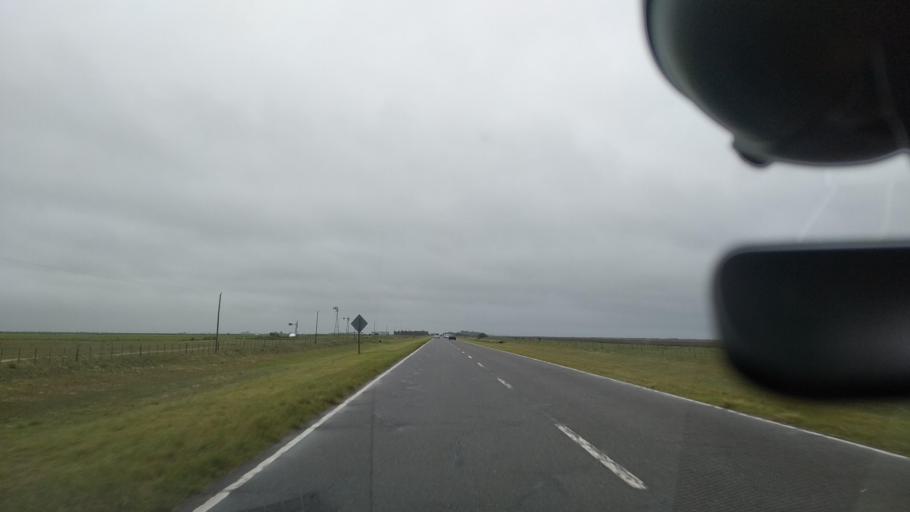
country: AR
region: Buenos Aires
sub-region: Partido de Dolores
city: Dolores
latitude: -36.0878
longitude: -57.4366
